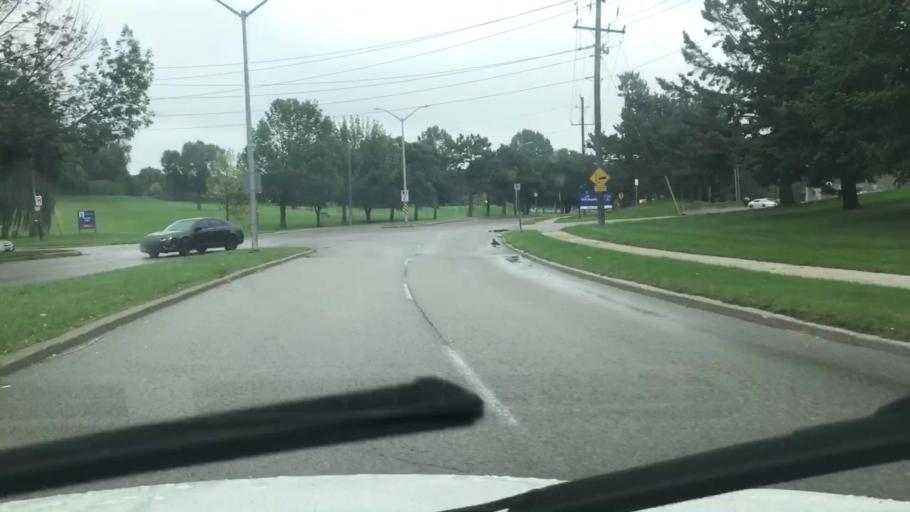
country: CA
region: Ontario
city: Newmarket
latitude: 44.0406
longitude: -79.4638
